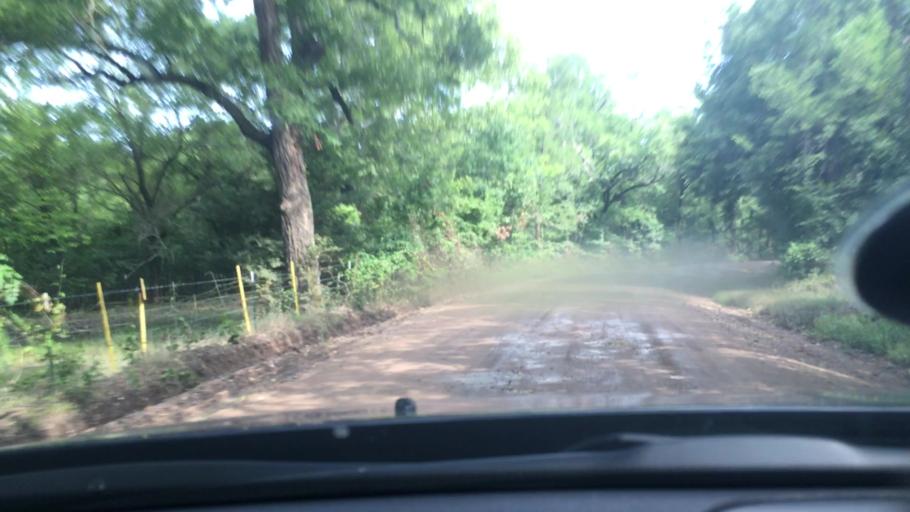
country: US
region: Oklahoma
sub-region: Atoka County
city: Atoka
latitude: 34.4472
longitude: -96.0675
